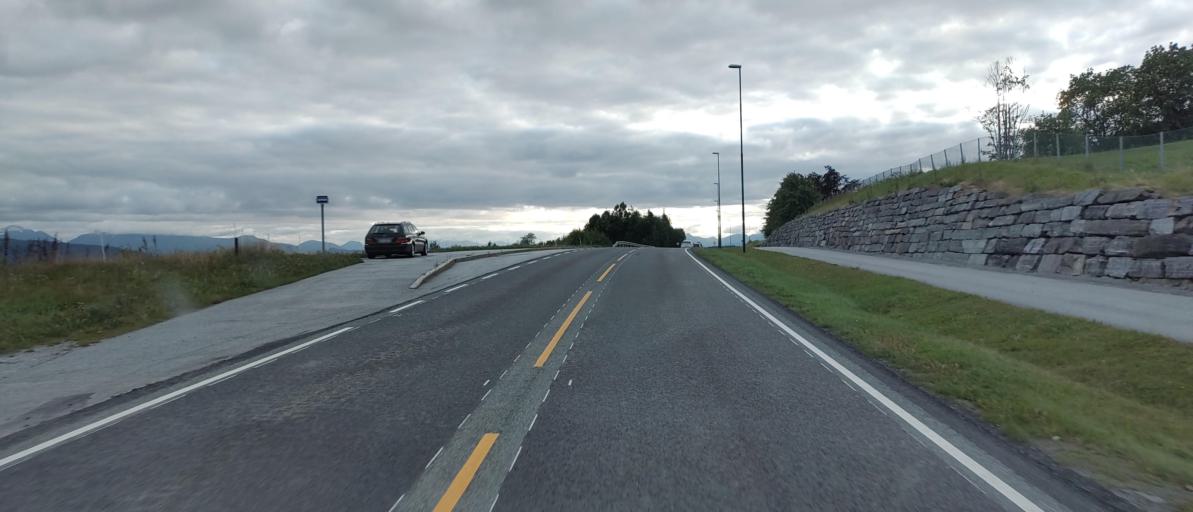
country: NO
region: More og Romsdal
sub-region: Molde
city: Hjelset
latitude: 62.7333
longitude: 7.4135
